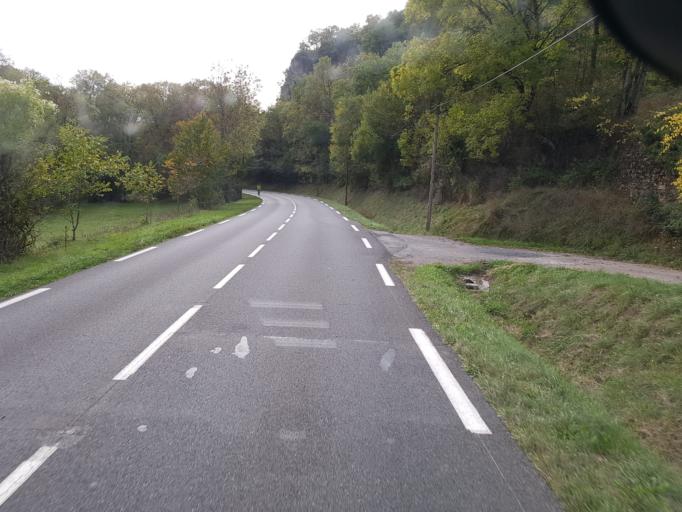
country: FR
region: Midi-Pyrenees
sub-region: Departement de l'Aveyron
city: Saint-Affrique
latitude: 43.9702
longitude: 2.9007
